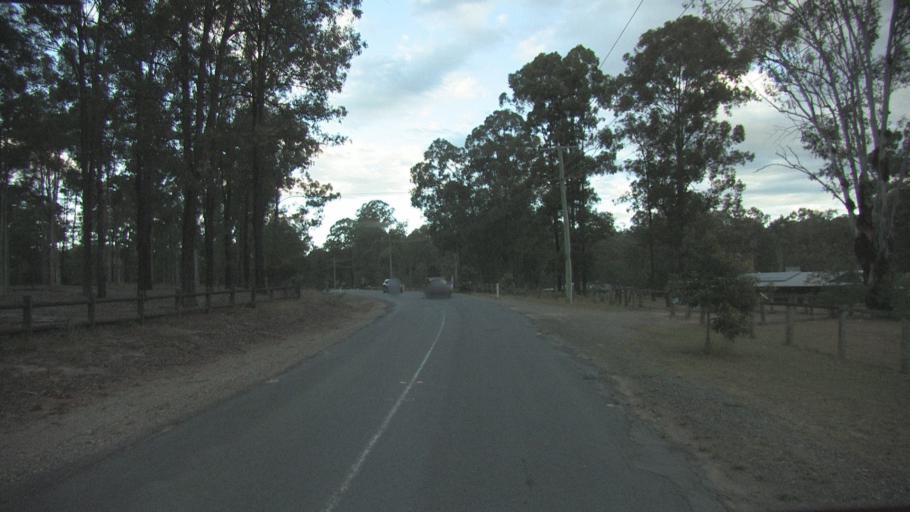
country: AU
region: Queensland
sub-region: Logan
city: Chambers Flat
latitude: -27.7887
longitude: 153.1360
